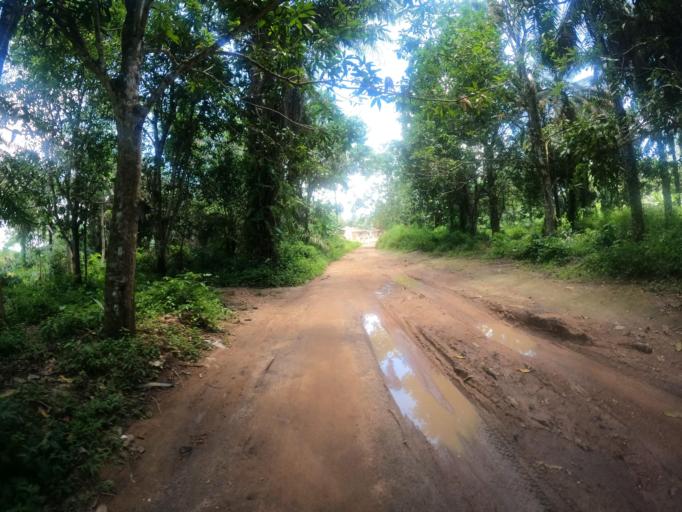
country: SL
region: Northern Province
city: Makeni
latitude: 8.8520
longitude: -12.1152
